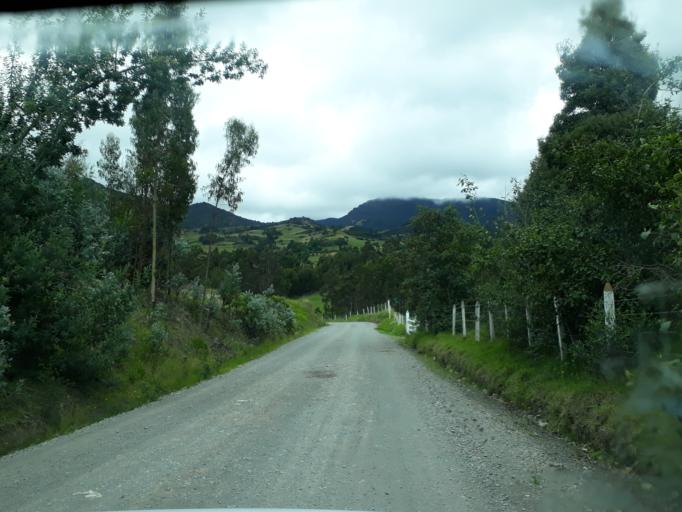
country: CO
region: Cundinamarca
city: La Mesa
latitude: 5.2877
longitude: -73.9076
